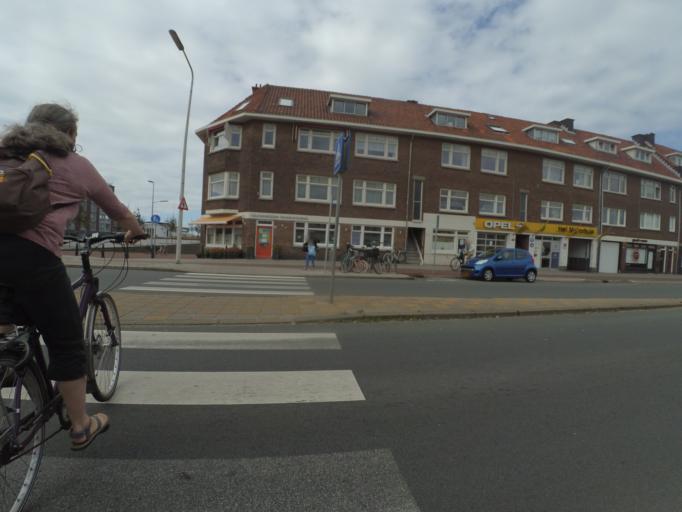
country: NL
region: South Holland
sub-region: Gemeente Den Haag
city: Scheveningen
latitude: 52.0972
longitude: 4.2710
